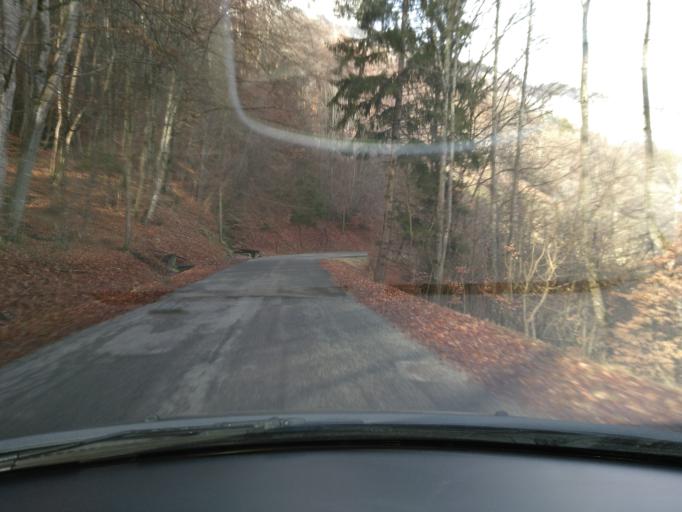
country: FR
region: Rhone-Alpes
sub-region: Departement de la Haute-Savoie
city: Sallanches
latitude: 45.9615
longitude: 6.6122
